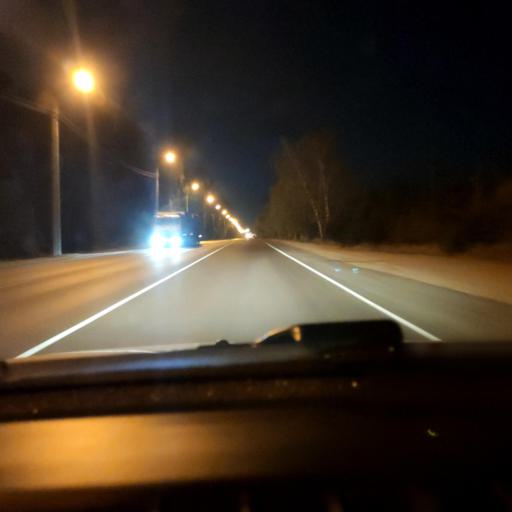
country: RU
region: Voronezj
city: Voronezh
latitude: 51.6795
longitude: 39.2738
